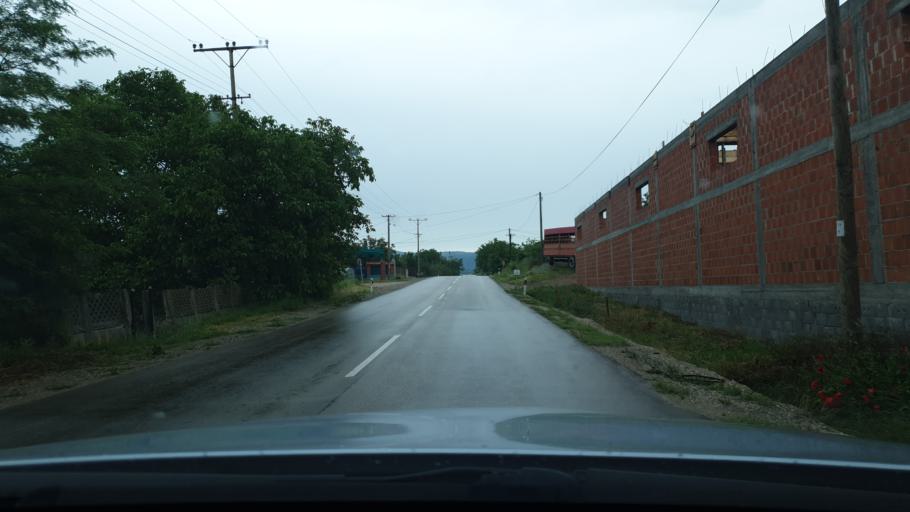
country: RS
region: Central Serbia
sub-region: Nisavski Okrug
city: Aleksinac
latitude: 43.6031
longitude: 21.6869
